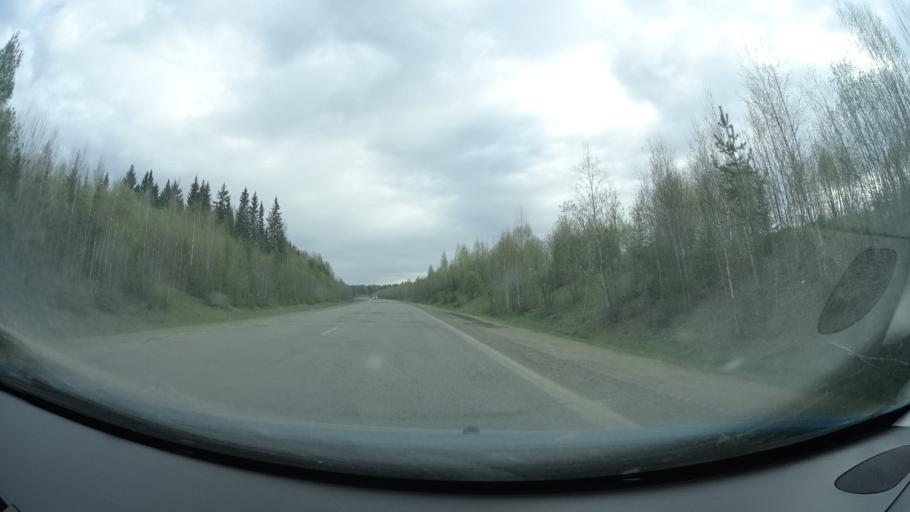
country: RU
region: Perm
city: Yugo-Kamskiy
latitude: 57.7690
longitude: 55.7490
